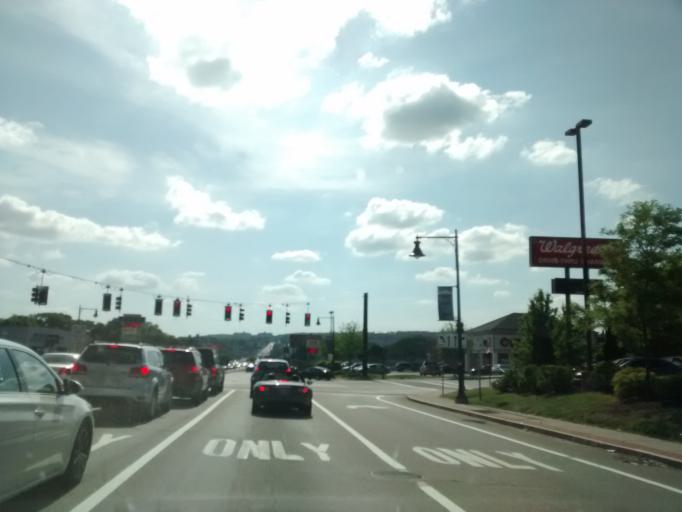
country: US
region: Massachusetts
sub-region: Worcester County
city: Hamilton
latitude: 42.2753
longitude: -71.7440
